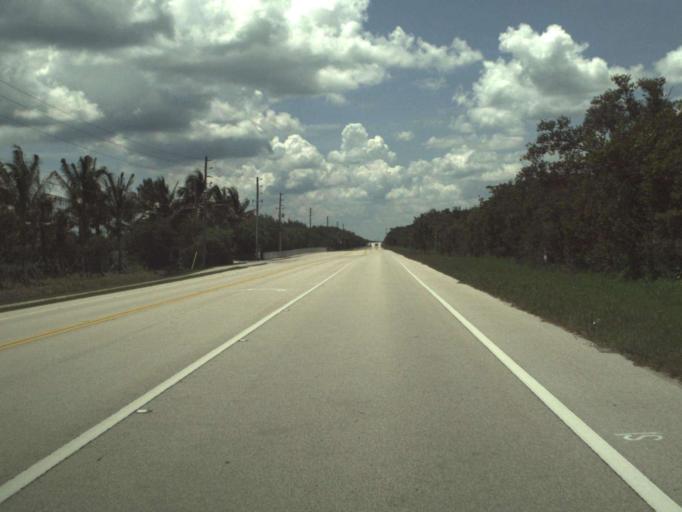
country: US
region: Florida
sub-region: Saint Lucie County
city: Indian River Estates
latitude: 27.3893
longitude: -80.2607
